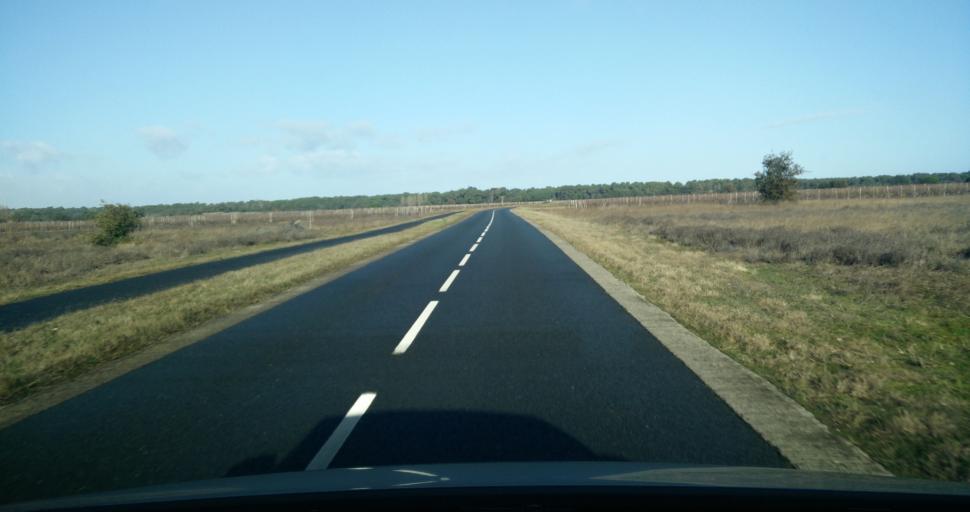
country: FR
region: Poitou-Charentes
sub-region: Departement de la Charente-Maritime
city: Sainte-Marie-de-Re
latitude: 46.1612
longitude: -1.3203
